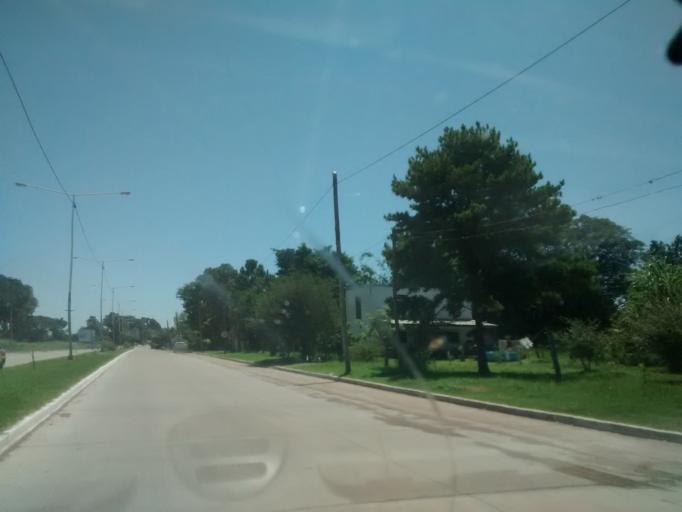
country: AR
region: Chaco
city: Fontana
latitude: -27.4139
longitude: -59.0326
